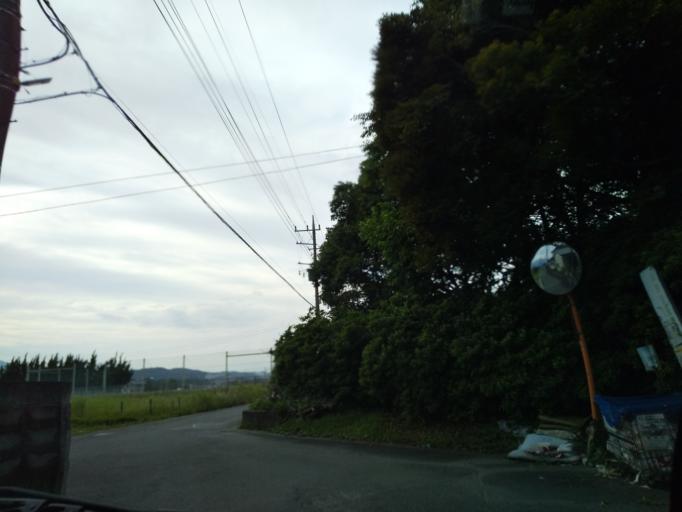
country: JP
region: Kanagawa
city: Zama
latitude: 35.4744
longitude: 139.3604
